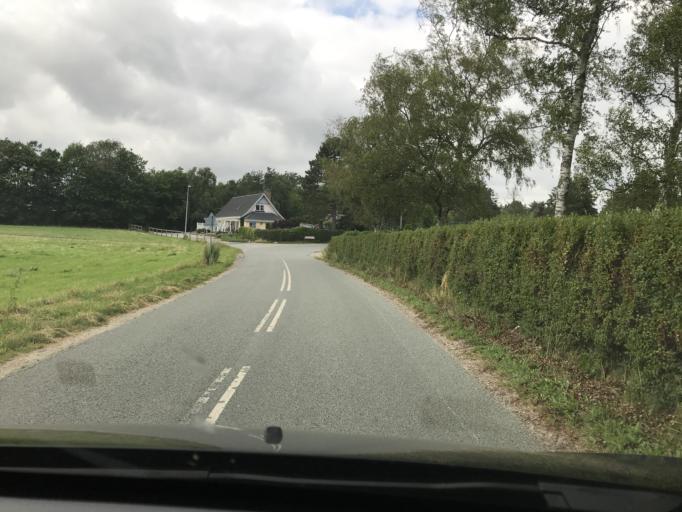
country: DK
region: Central Jutland
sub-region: Syddjurs Kommune
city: Ronde
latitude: 56.3550
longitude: 10.4485
